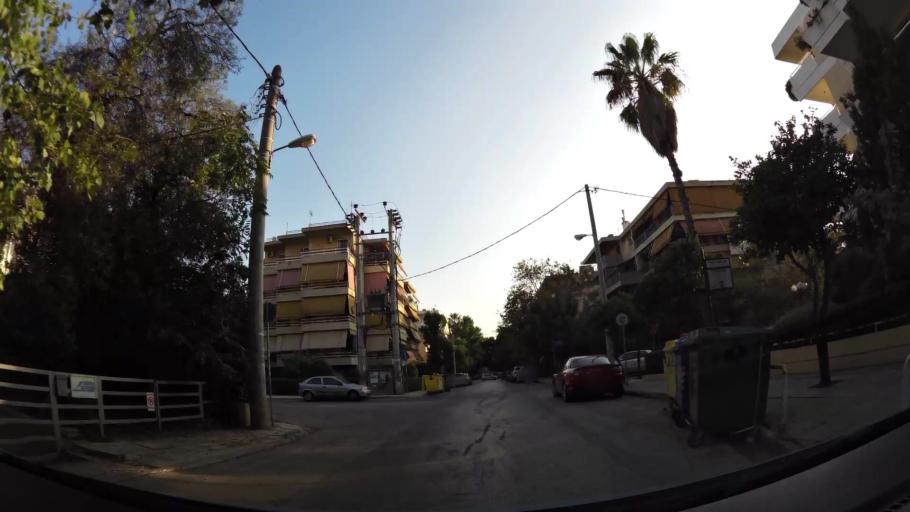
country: GR
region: Attica
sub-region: Nomarchia Athinas
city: Khalandrion
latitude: 38.0161
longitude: 23.8068
